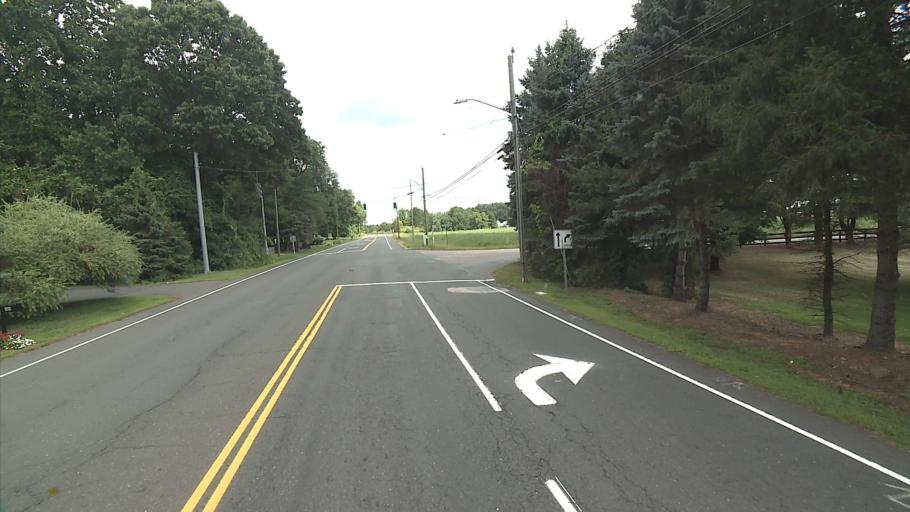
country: US
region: Connecticut
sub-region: Hartford County
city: Tariffville
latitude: 41.8778
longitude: -72.7442
